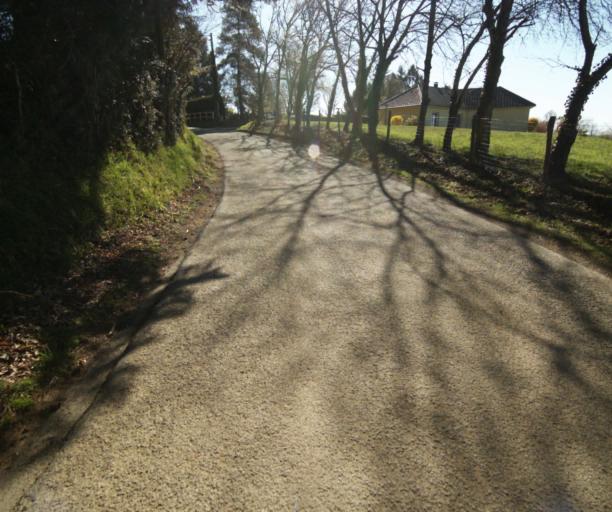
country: FR
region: Limousin
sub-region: Departement de la Correze
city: Seilhac
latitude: 45.3715
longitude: 1.7417
